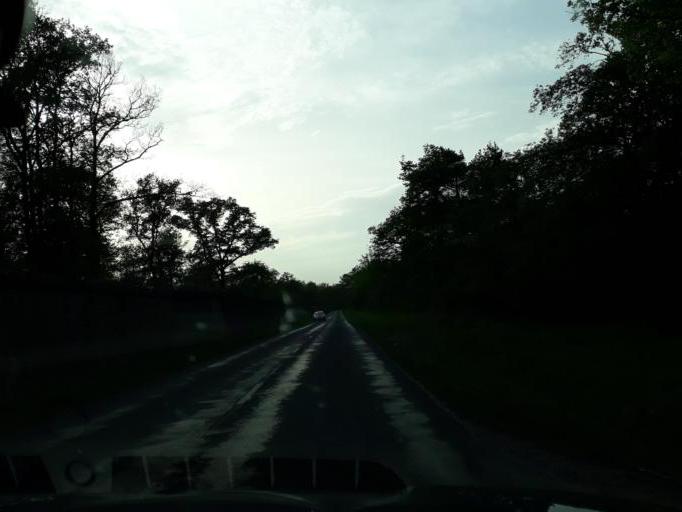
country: FR
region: Centre
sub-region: Departement du Loir-et-Cher
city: Muides-sur-Loire
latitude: 47.6554
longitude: 1.5555
